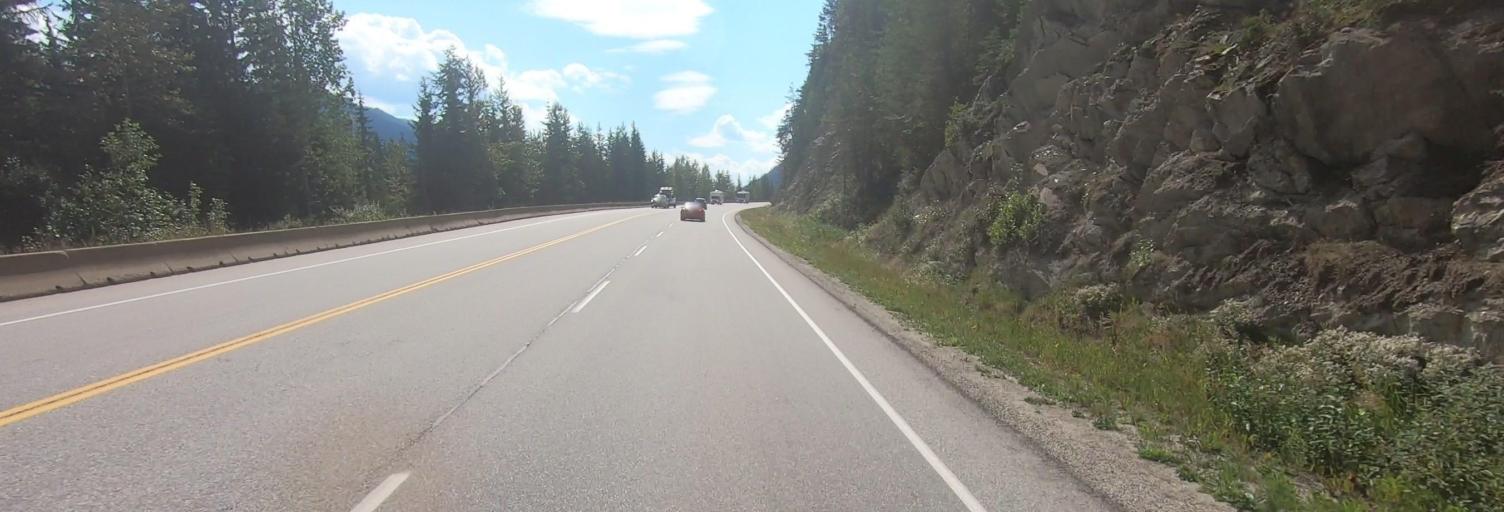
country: CA
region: British Columbia
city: Golden
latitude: 51.3630
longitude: -117.4400
